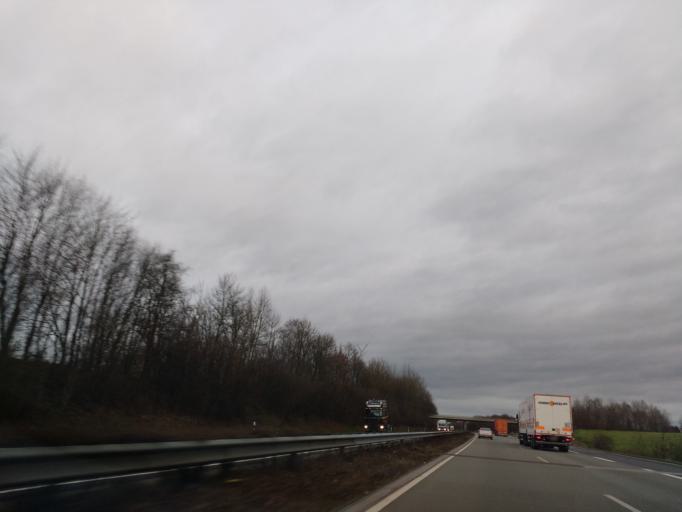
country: DE
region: Lower Saxony
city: Buchholz in der Nordheide
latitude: 53.3812
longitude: 9.8699
